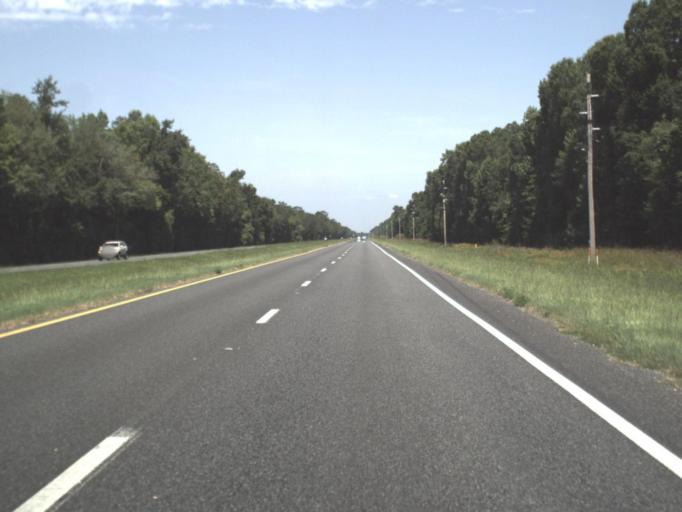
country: US
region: Florida
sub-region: Dixie County
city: Cross City
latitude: 29.6666
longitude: -83.2155
